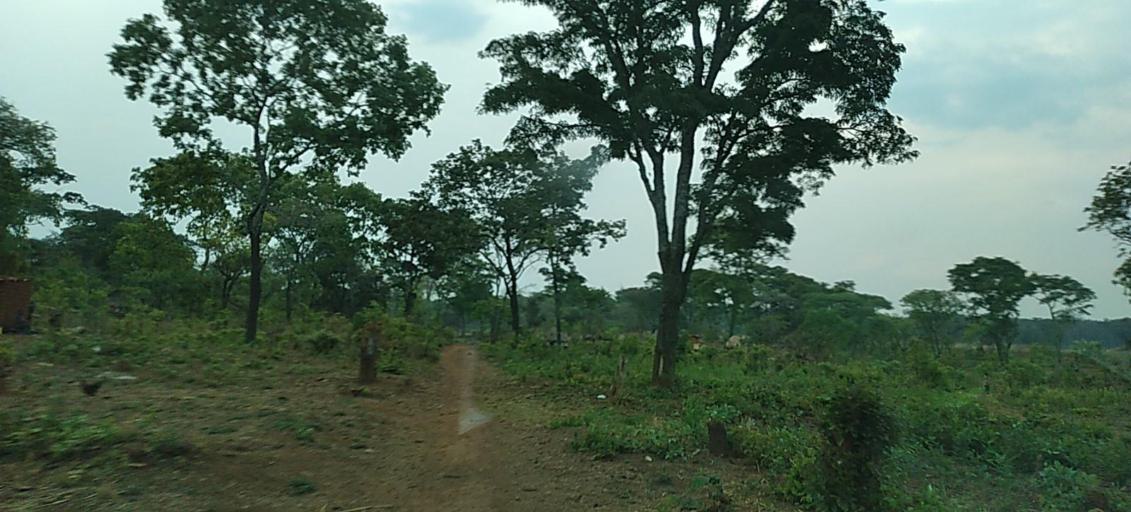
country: ZM
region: North-Western
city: Solwezi
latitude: -12.0441
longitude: 26.0050
